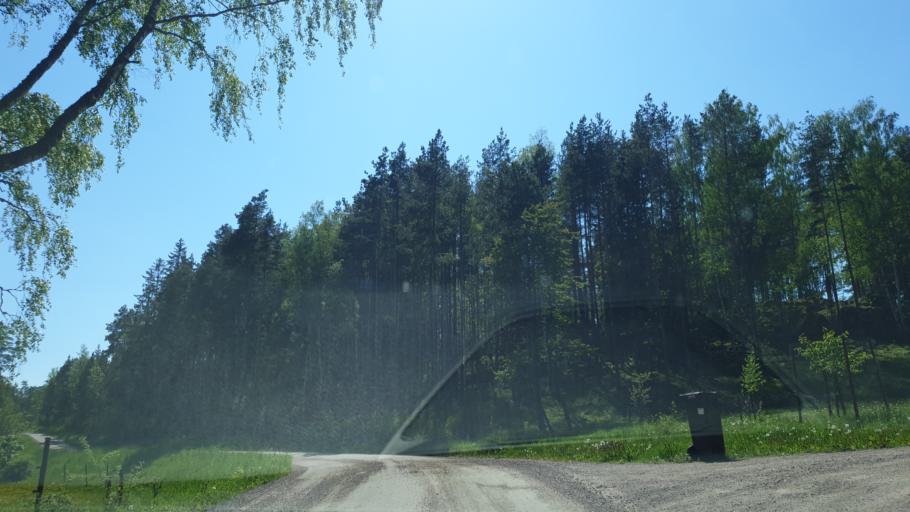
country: SE
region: Soedermanland
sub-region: Trosa Kommun
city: Vagnharad
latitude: 58.9280
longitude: 17.5157
